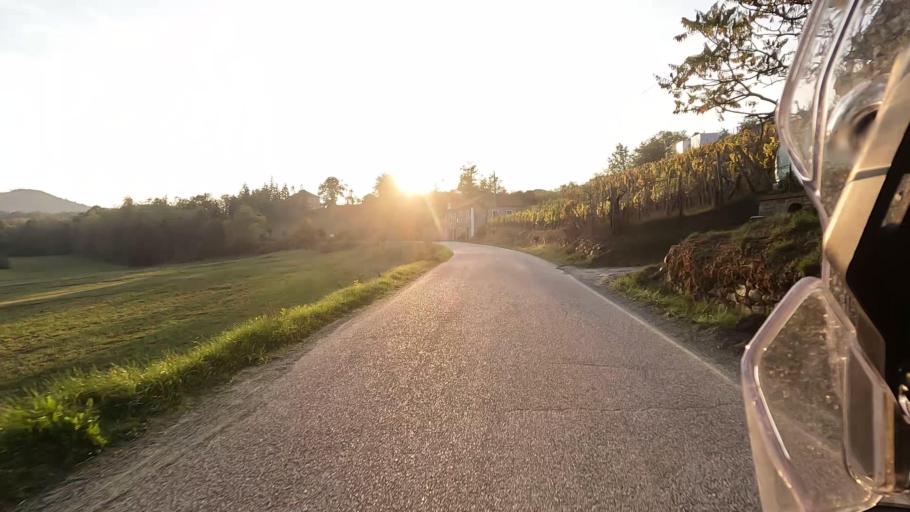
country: IT
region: Liguria
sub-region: Provincia di Savona
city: Mioglia
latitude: 44.5163
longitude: 8.4567
